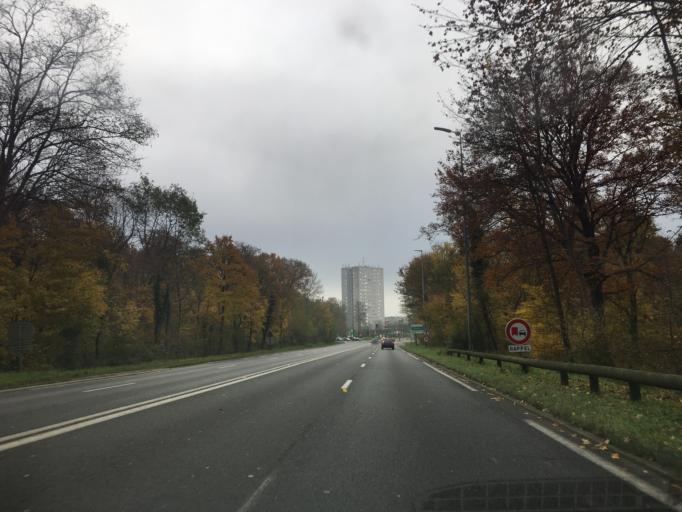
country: FR
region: Ile-de-France
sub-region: Departement de Seine-et-Marne
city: Fontainebleau
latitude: 48.4104
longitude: 2.6835
